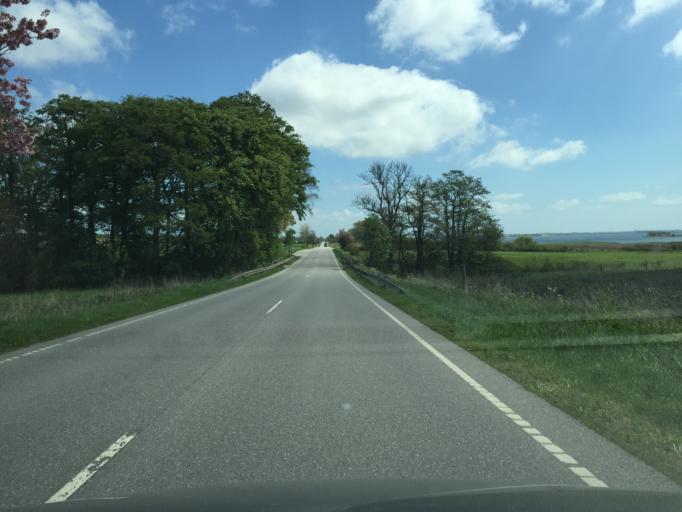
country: DK
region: Zealand
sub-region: Guldborgsund Kommune
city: Stubbekobing
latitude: 54.9977
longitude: 12.1084
